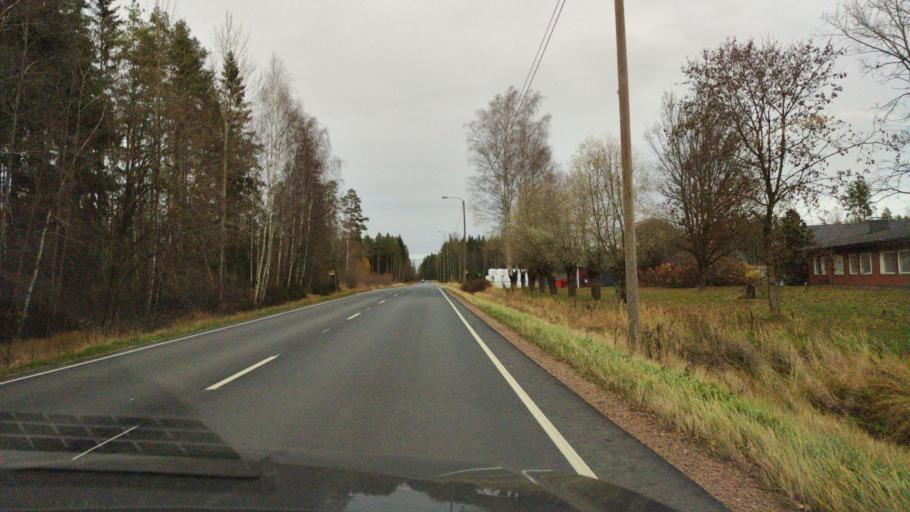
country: FI
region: Varsinais-Suomi
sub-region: Turku
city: Vahto
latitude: 60.6577
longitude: 22.4323
